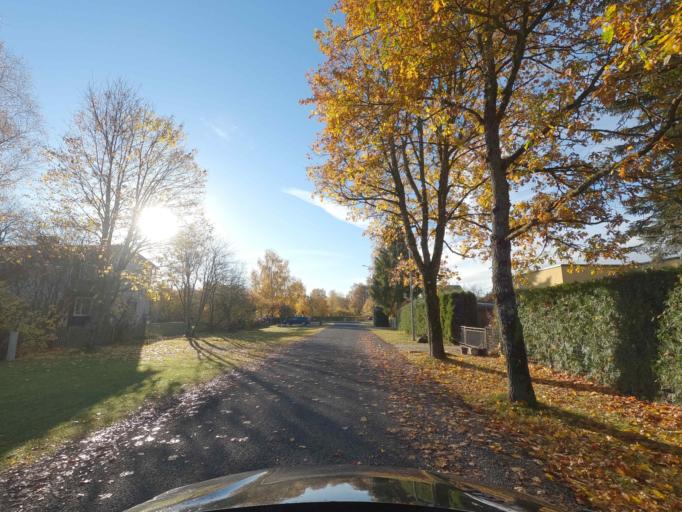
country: EE
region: Raplamaa
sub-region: Kohila vald
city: Kohila
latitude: 59.1633
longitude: 24.7679
